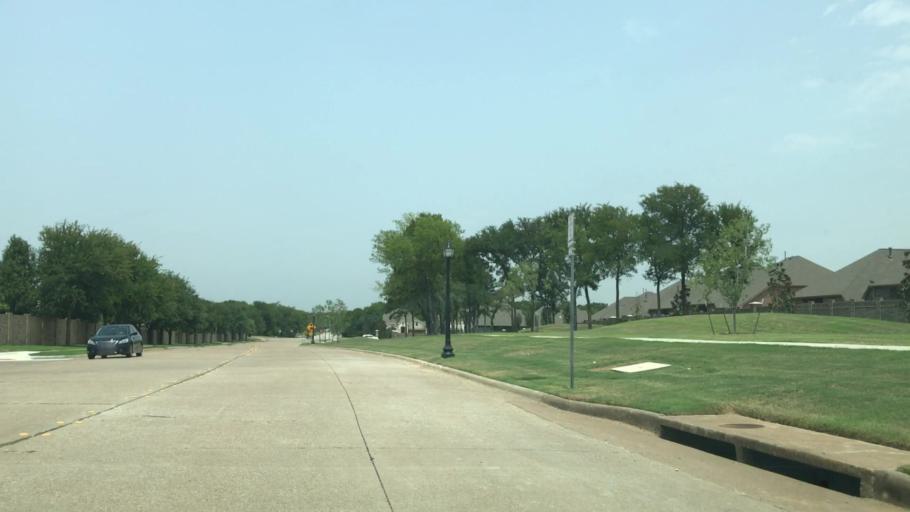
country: US
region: Texas
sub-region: Tarrant County
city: Euless
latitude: 32.8440
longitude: -97.0725
